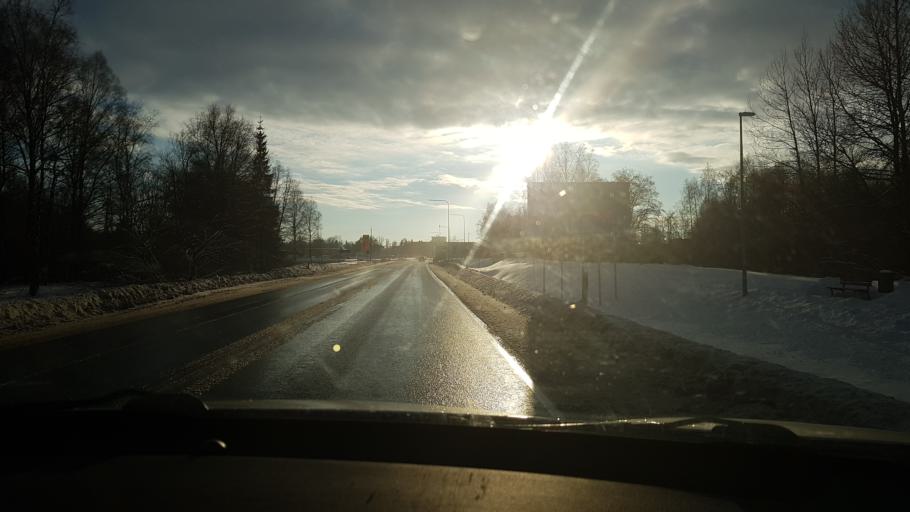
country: EE
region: Jaervamaa
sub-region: Paide linn
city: Paide
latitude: 58.8978
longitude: 25.5730
